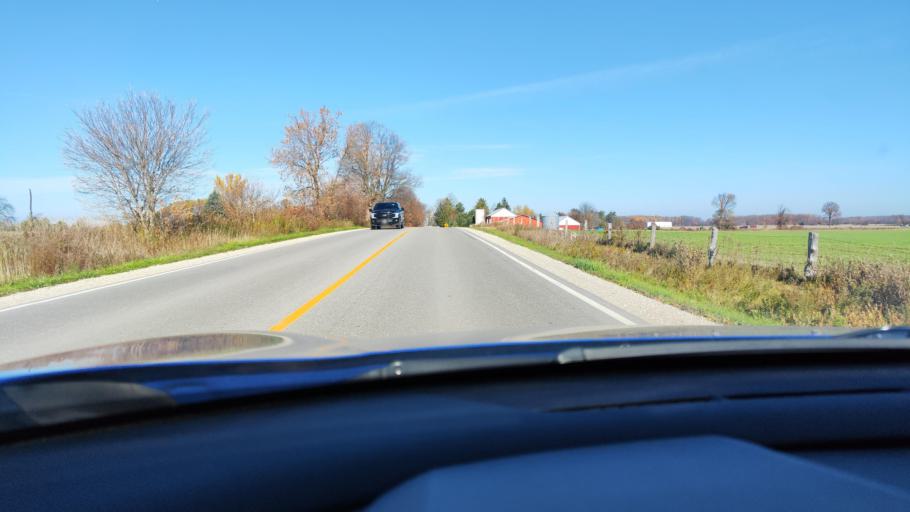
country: CA
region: Ontario
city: Wasaga Beach
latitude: 44.4185
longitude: -80.0620
